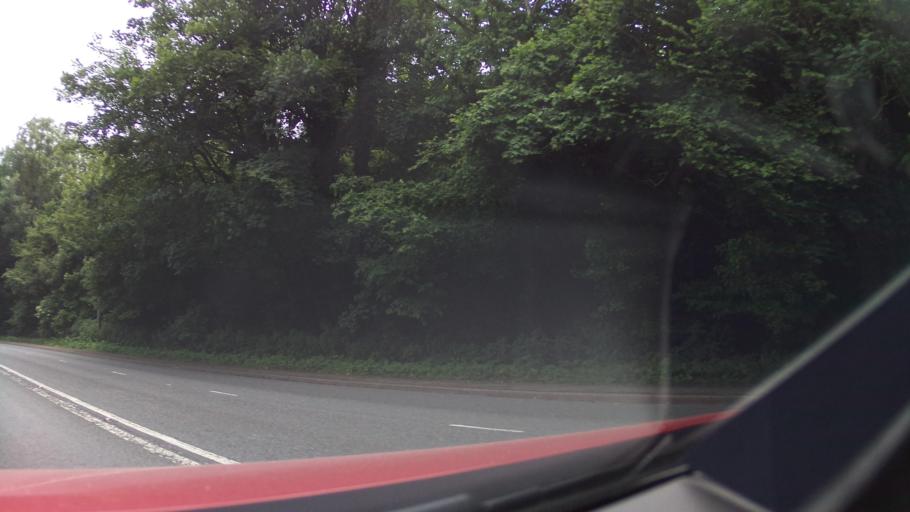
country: GB
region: Wales
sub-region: Cardiff
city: Radyr
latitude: 51.4646
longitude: -3.2804
